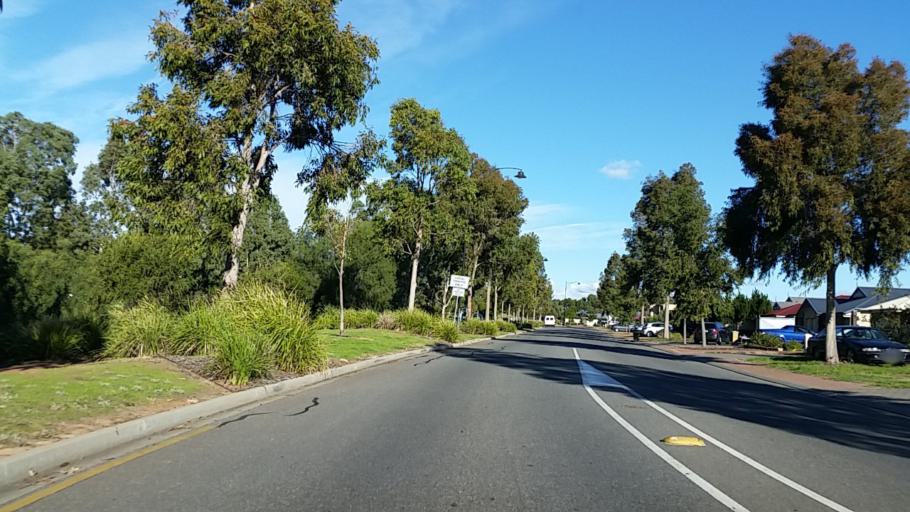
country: AU
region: South Australia
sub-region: Playford
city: Smithfield
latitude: -34.6846
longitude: 138.6800
